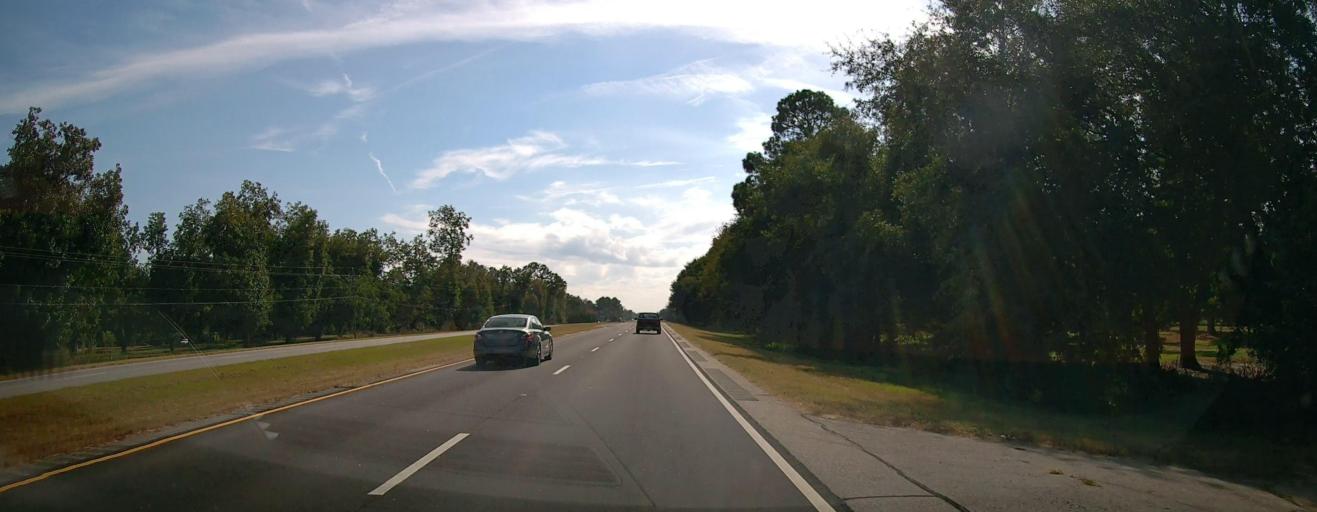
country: US
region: Georgia
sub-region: Dougherty County
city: Putney
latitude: 31.3903
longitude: -84.1474
